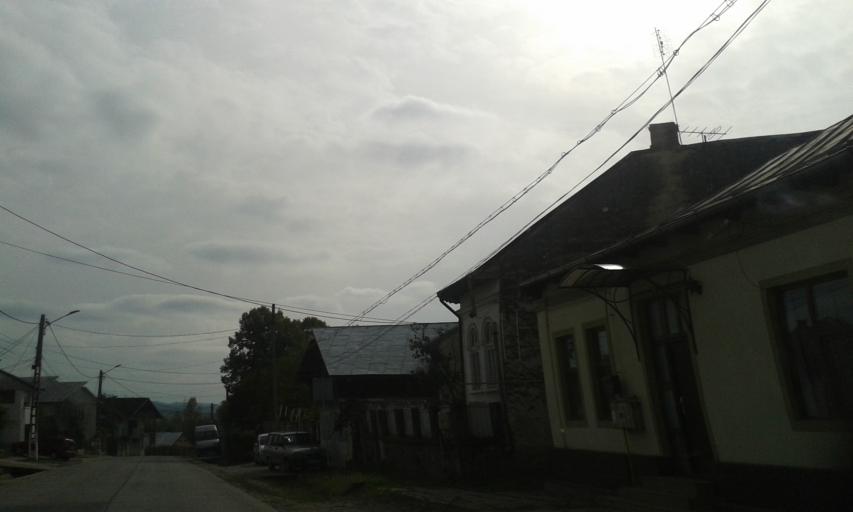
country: RO
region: Gorj
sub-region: Comuna Targu Carbunesti
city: Targu Carbunesti
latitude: 44.9521
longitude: 23.5135
